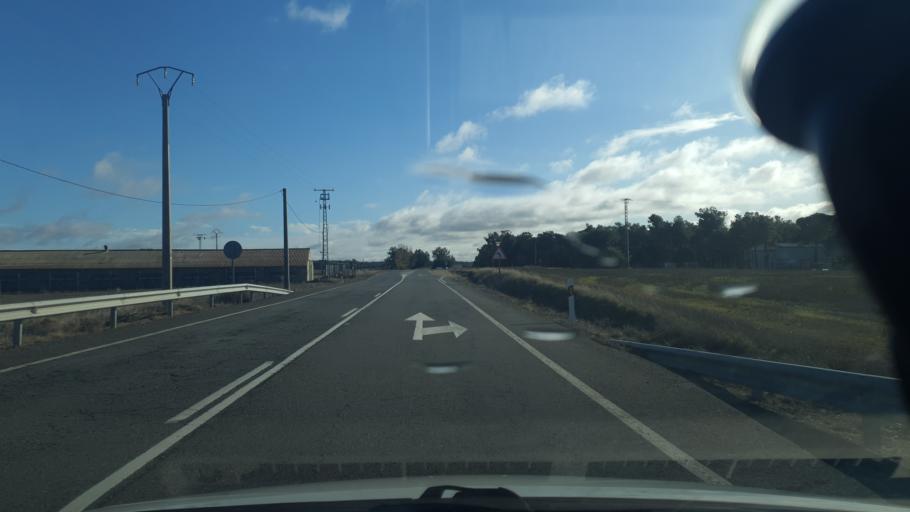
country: ES
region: Castille and Leon
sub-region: Provincia de Segovia
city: Martin Munoz de la Dehesa
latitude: 41.0466
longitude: -4.6852
